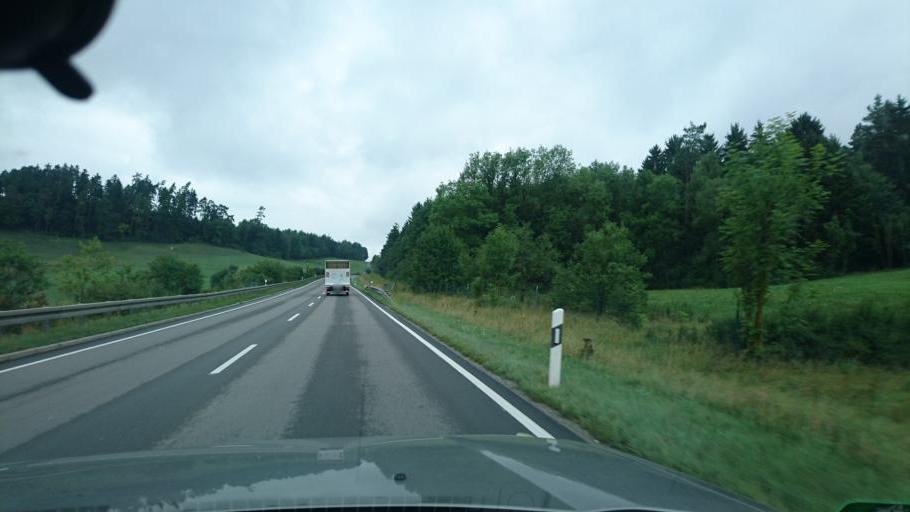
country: DE
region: Baden-Wuerttemberg
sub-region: Freiburg Region
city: Rottweil
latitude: 48.1346
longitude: 8.6361
